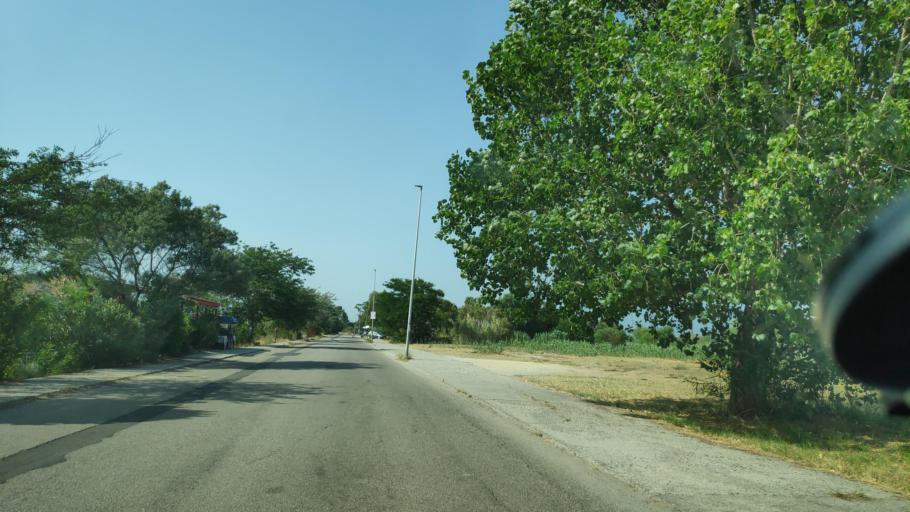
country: IT
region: Calabria
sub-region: Provincia di Catanzaro
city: Badolato Marina
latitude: 38.5765
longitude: 16.5683
